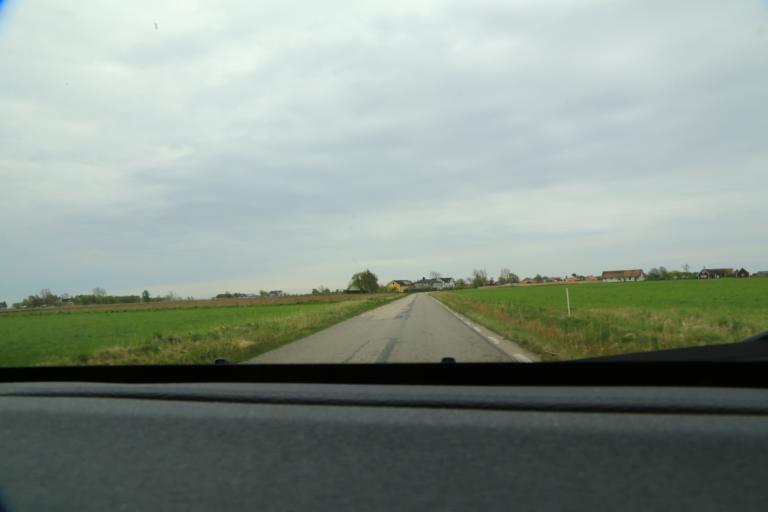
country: SE
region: Halland
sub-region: Varbergs Kommun
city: Traslovslage
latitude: 57.0324
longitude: 12.3252
